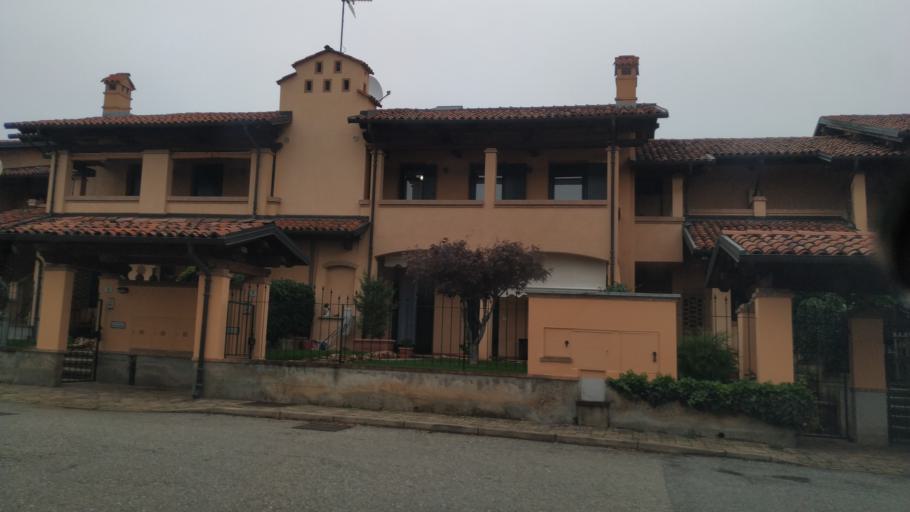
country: IT
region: Piedmont
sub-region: Provincia di Biella
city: Lessona
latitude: 45.5848
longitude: 8.1954
